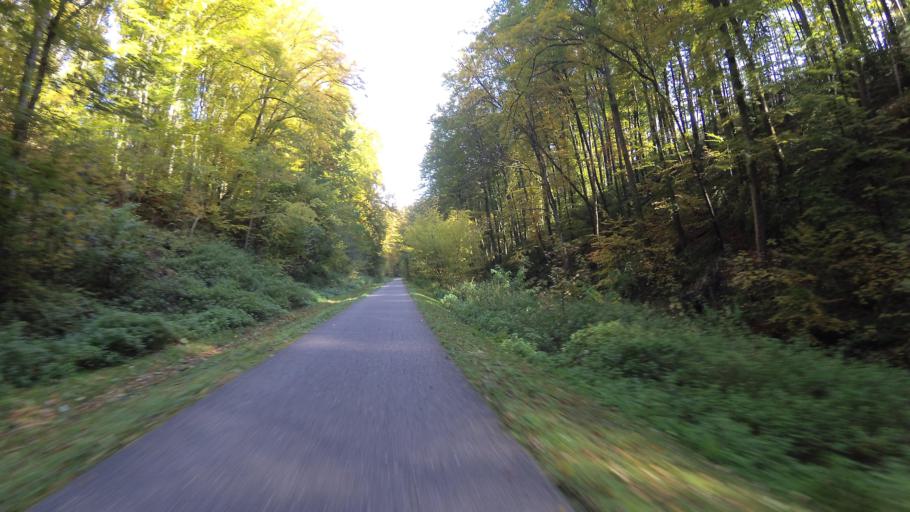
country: DE
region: Baden-Wuerttemberg
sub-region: Regierungsbezirk Stuttgart
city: Kuenzelsau
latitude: 49.2608
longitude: 9.7046
